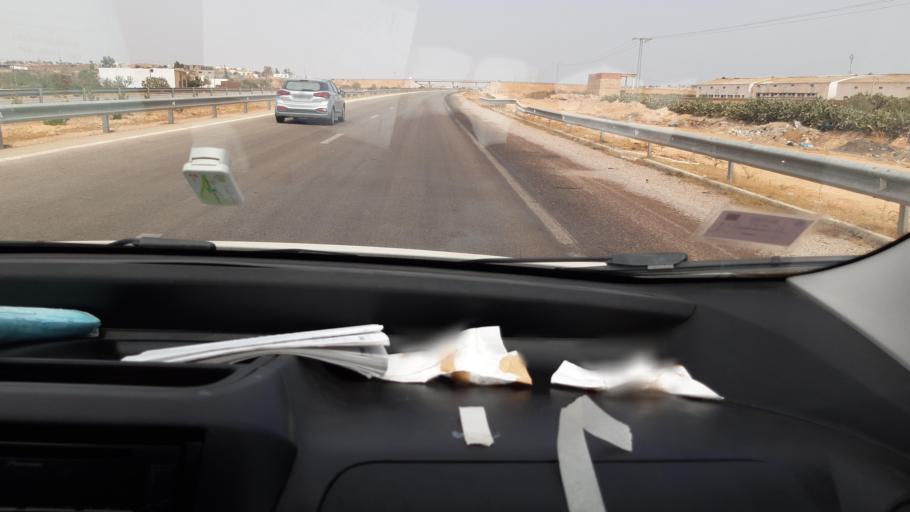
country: TN
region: Safaqis
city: Sfax
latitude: 34.8348
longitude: 10.6558
